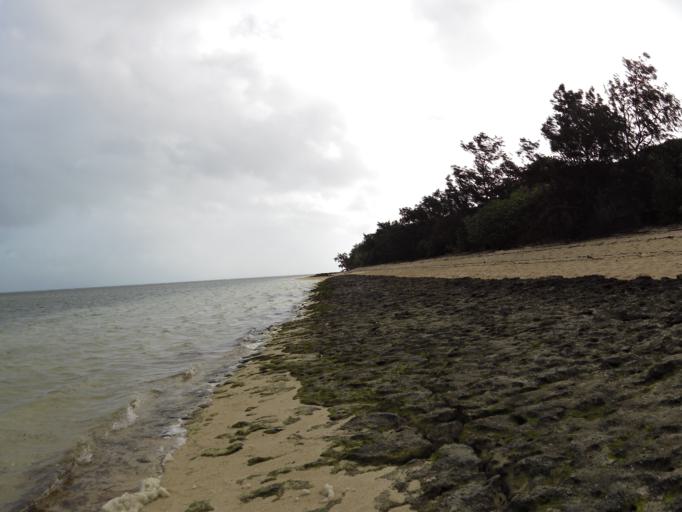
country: AU
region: Queensland
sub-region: Cairns
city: Yorkeys Knob
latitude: -16.7607
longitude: 145.9761
